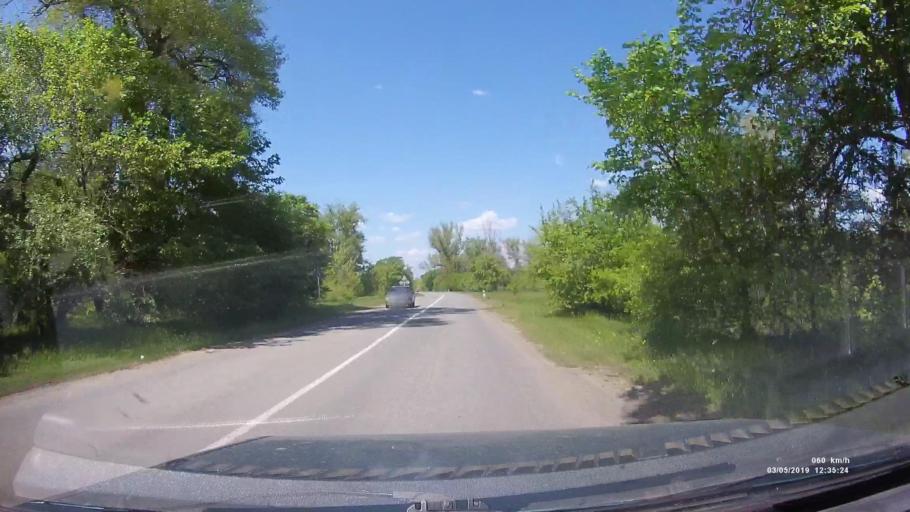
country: RU
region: Rostov
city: Semikarakorsk
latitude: 47.5264
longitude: 40.7612
